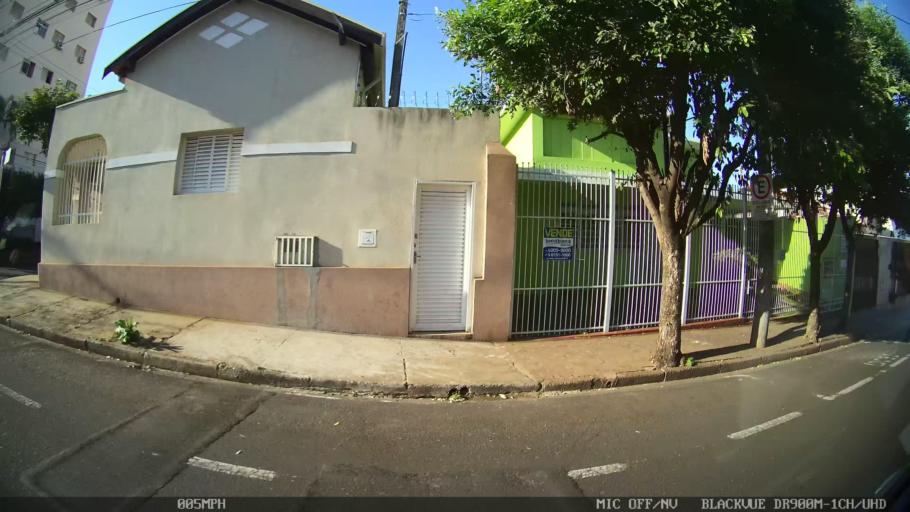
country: BR
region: Sao Paulo
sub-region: Sao Jose Do Rio Preto
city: Sao Jose do Rio Preto
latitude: -20.8066
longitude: -49.3857
